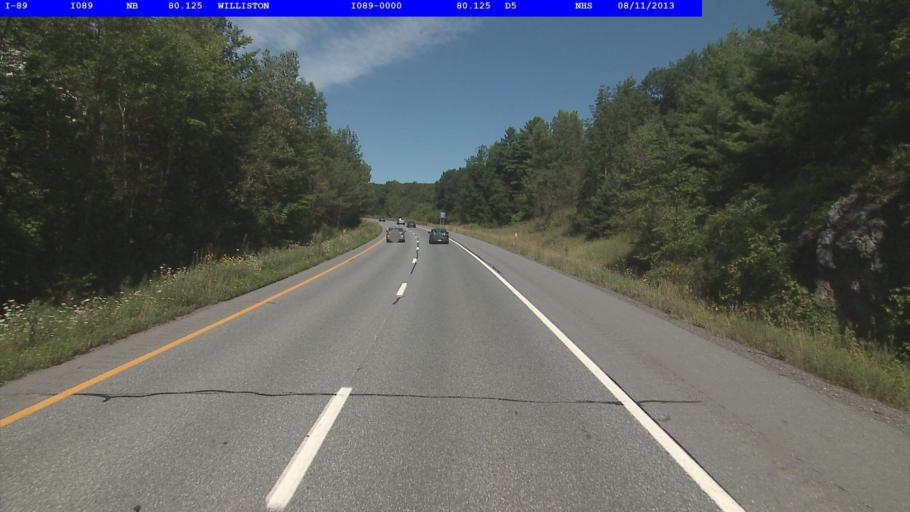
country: US
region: Vermont
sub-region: Chittenden County
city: Williston
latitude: 44.4314
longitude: -73.0389
